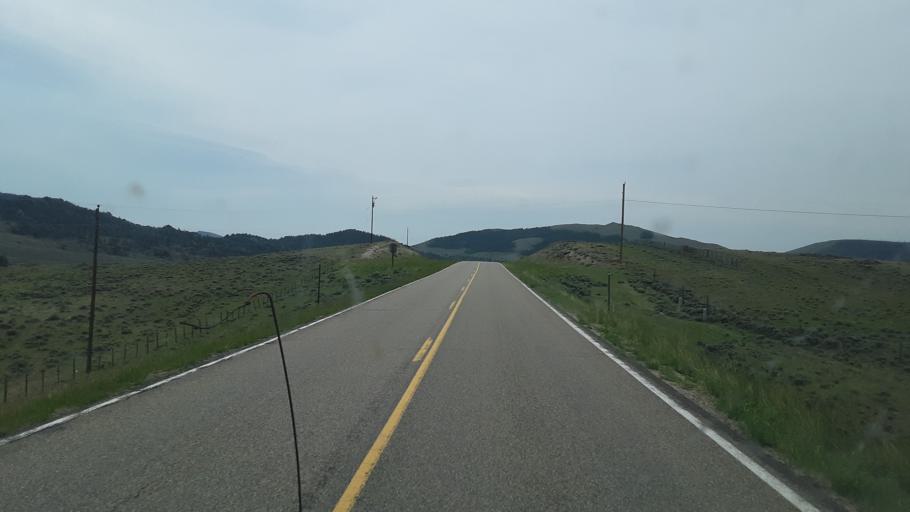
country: US
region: Colorado
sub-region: Jackson County
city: Walden
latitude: 40.9494
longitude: -106.3523
